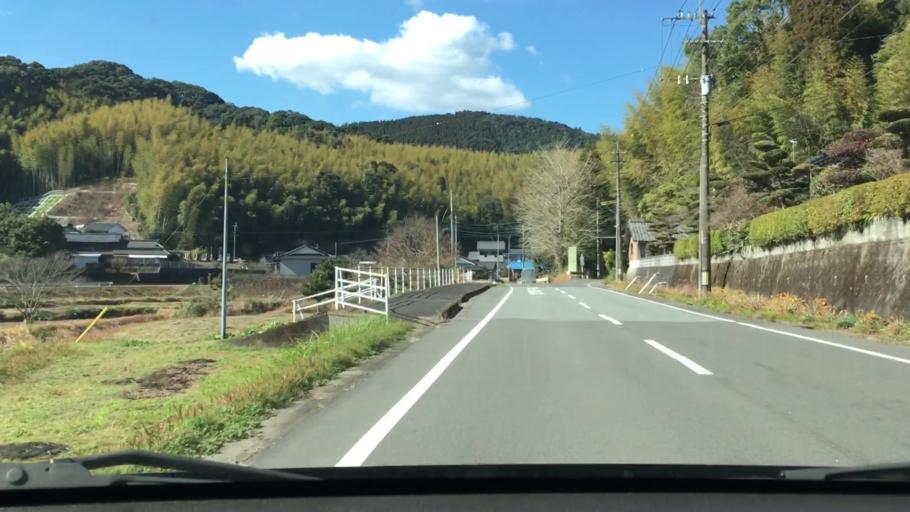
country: JP
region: Kagoshima
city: Ijuin
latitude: 31.7071
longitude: 130.4436
